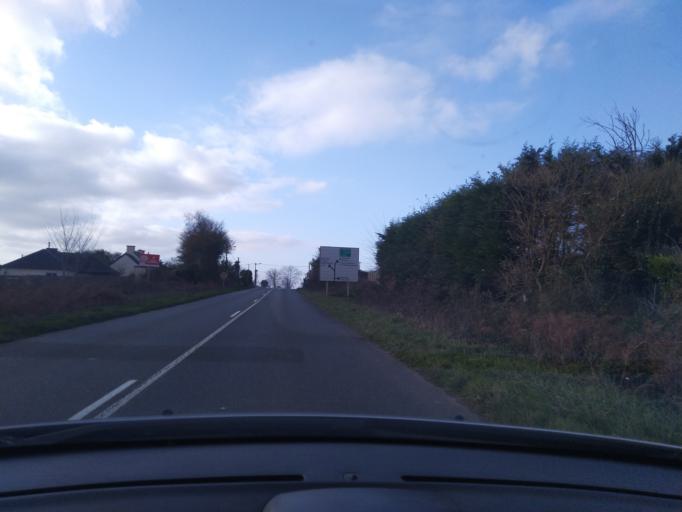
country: FR
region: Brittany
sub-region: Departement du Finistere
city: Morlaix
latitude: 48.5782
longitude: -3.7915
